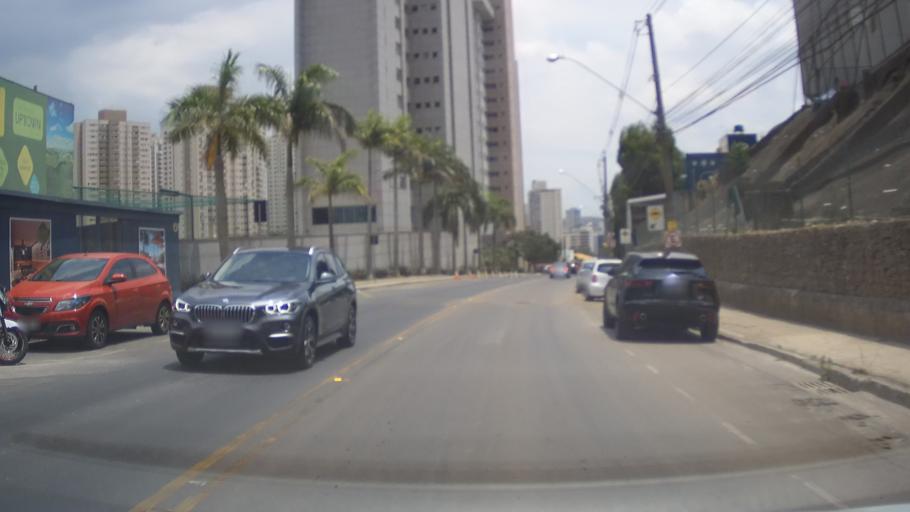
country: BR
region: Minas Gerais
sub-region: Belo Horizonte
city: Belo Horizonte
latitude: -19.9735
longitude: -43.9311
